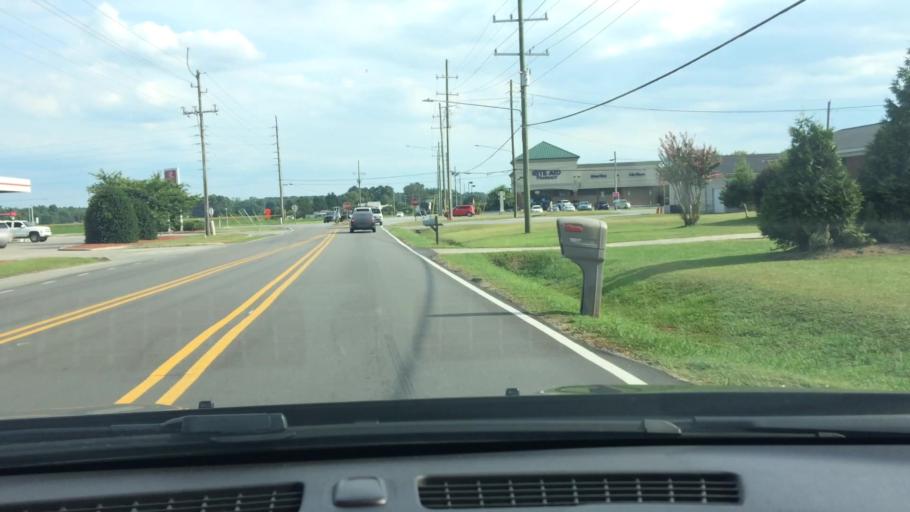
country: US
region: North Carolina
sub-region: Pitt County
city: Winterville
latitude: 35.5260
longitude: -77.3849
